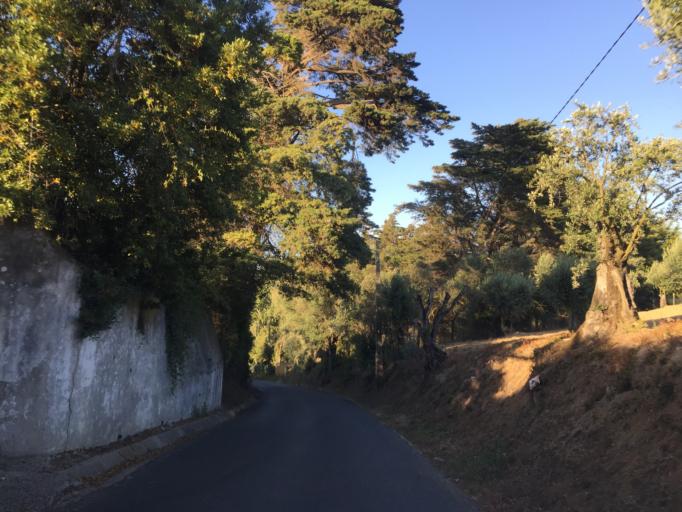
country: PT
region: Santarem
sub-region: Cartaxo
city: Pontevel
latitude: 39.1654
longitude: -8.8299
